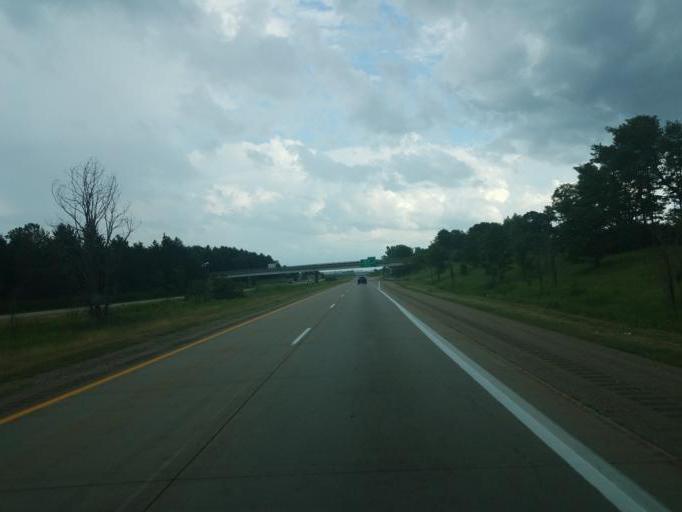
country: US
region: Michigan
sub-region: Calhoun County
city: Marshall
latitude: 42.2777
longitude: -84.9942
